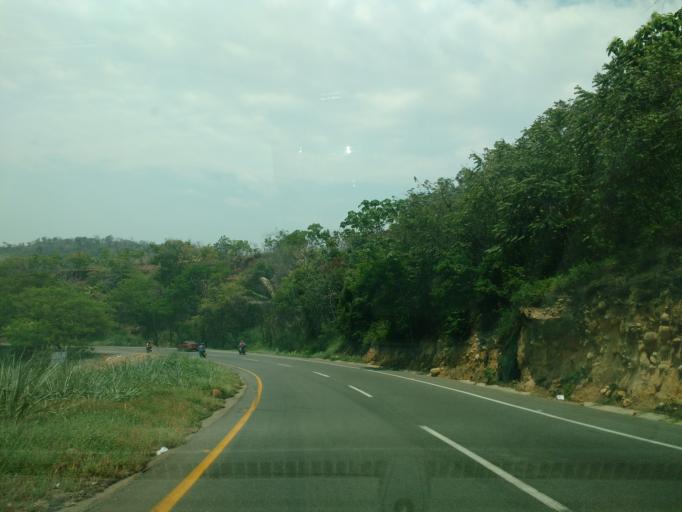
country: CO
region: Tolima
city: Melgar
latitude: 4.2083
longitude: -74.6533
